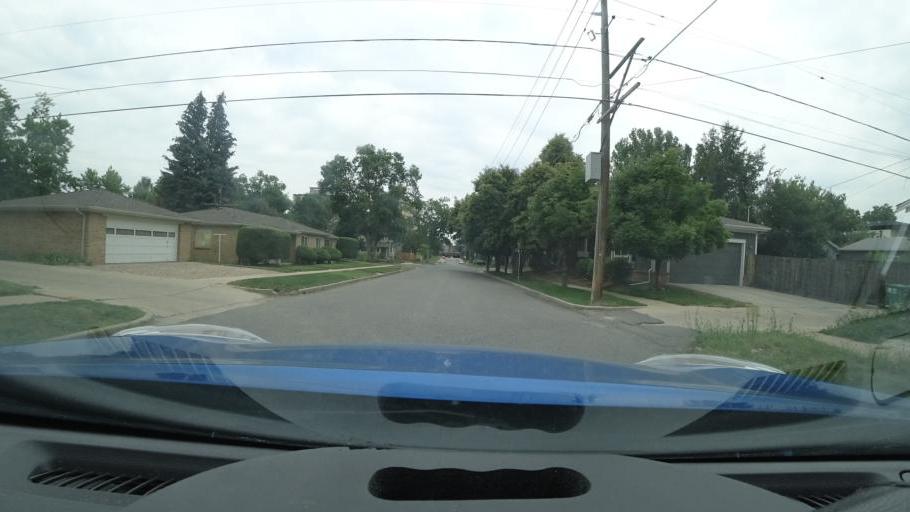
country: US
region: Colorado
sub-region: Arapahoe County
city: Glendale
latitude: 39.6839
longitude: -104.9683
